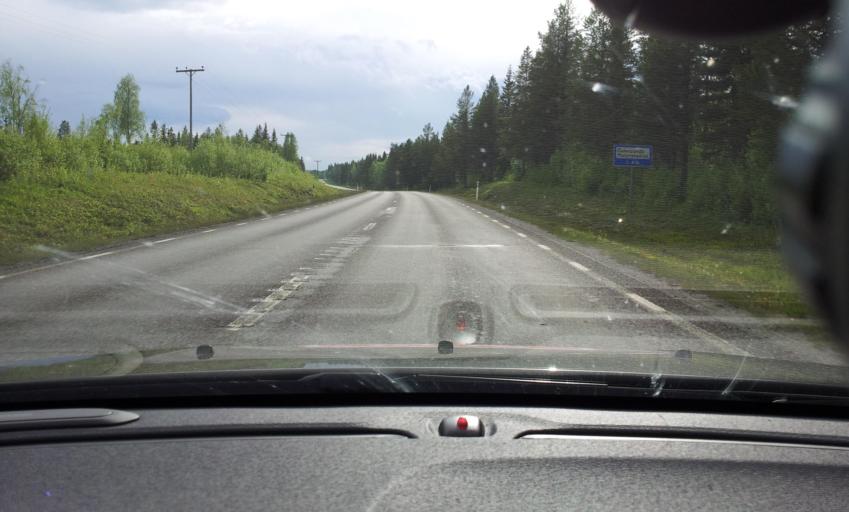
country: SE
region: Jaemtland
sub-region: OEstersunds Kommun
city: Lit
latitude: 63.2043
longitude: 14.8241
